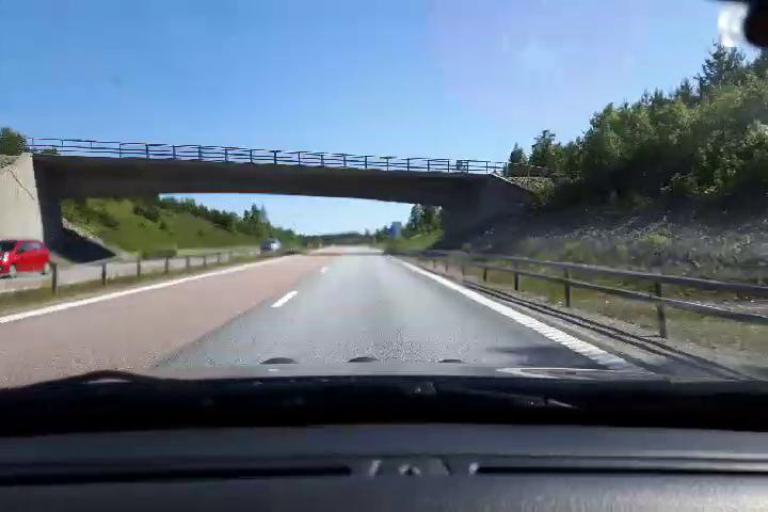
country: SE
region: Gaevleborg
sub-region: Hudiksvalls Kommun
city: Iggesund
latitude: 61.5213
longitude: 16.9765
